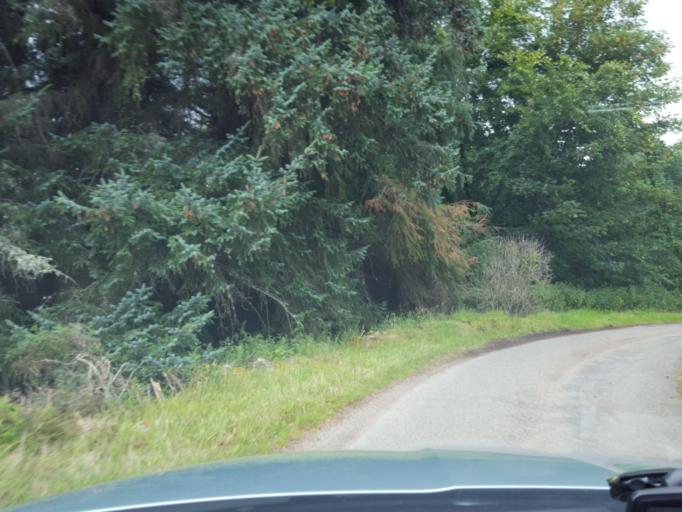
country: GB
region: Scotland
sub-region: Moray
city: Rothes
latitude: 57.4191
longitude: -3.3590
